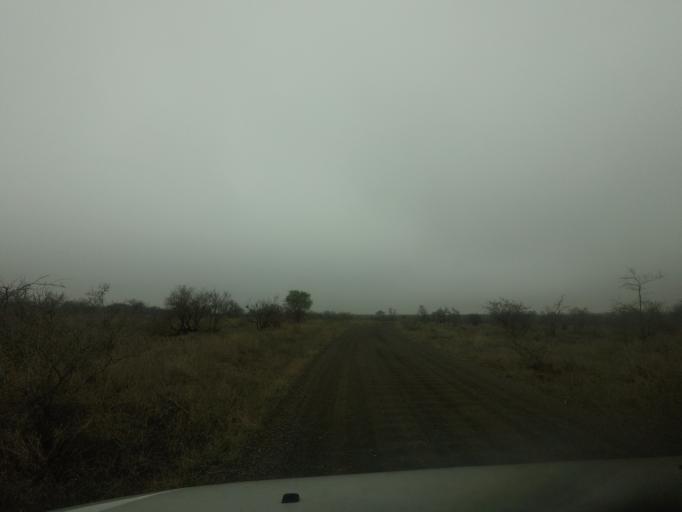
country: ZA
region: Limpopo
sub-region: Mopani District Municipality
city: Phalaborwa
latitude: -24.2623
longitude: 31.6574
